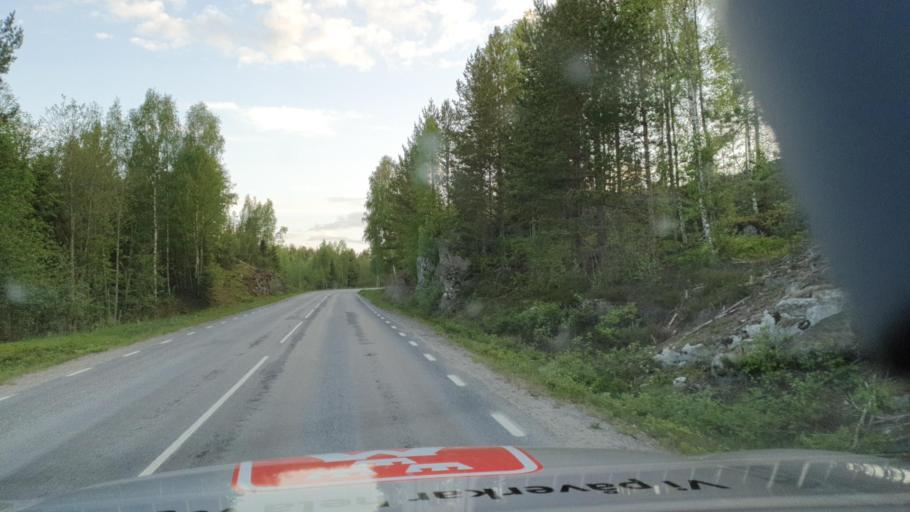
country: SE
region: Vaesternorrland
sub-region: OErnskoeldsviks Kommun
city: Ornskoldsvik
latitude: 63.2522
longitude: 18.6732
